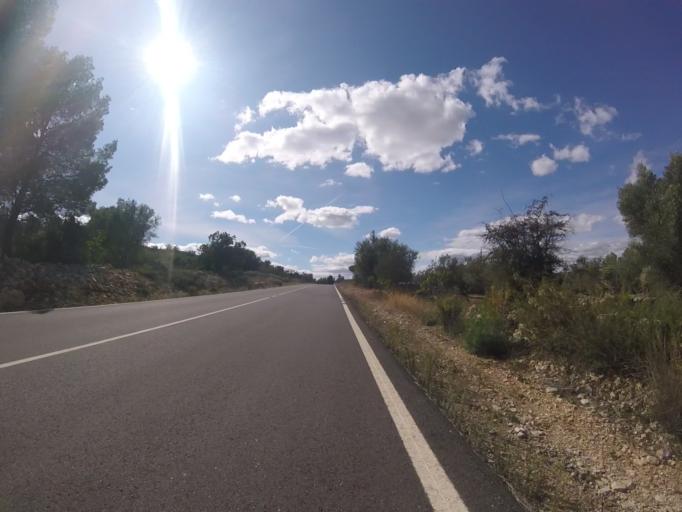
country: ES
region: Valencia
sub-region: Provincia de Castello
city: Cati
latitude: 40.4312
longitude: 0.0941
